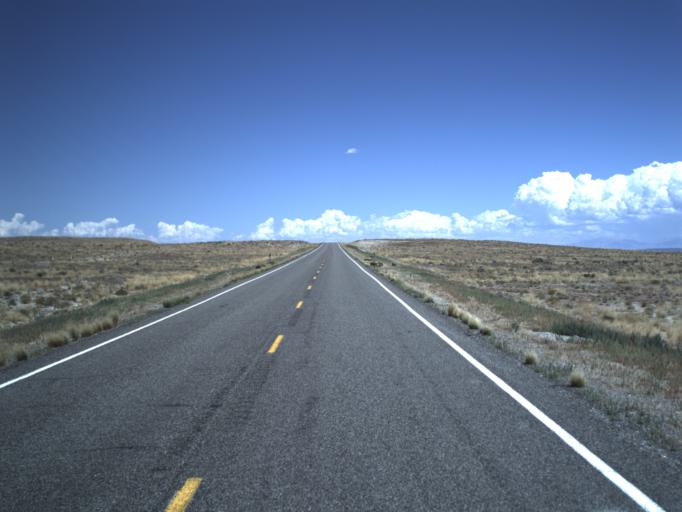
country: US
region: Utah
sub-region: Millard County
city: Delta
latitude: 39.1468
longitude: -113.0751
